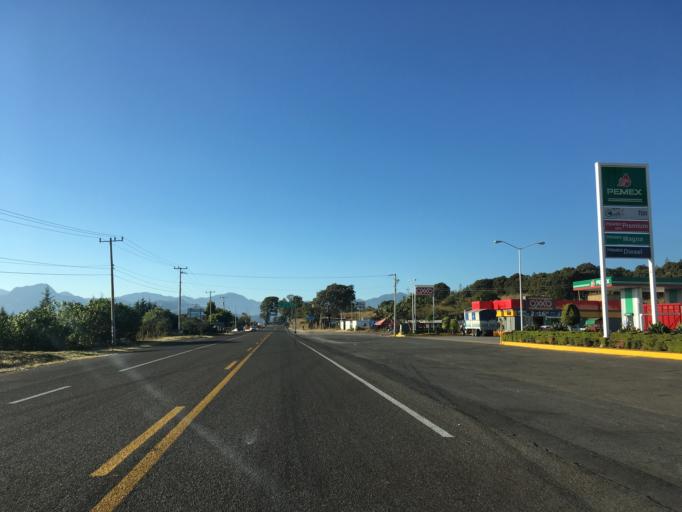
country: MX
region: Michoacan
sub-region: Zitacuaro
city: Puentecillas (Tercera Manzana de Zirahuato)
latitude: 19.4831
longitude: -100.4430
